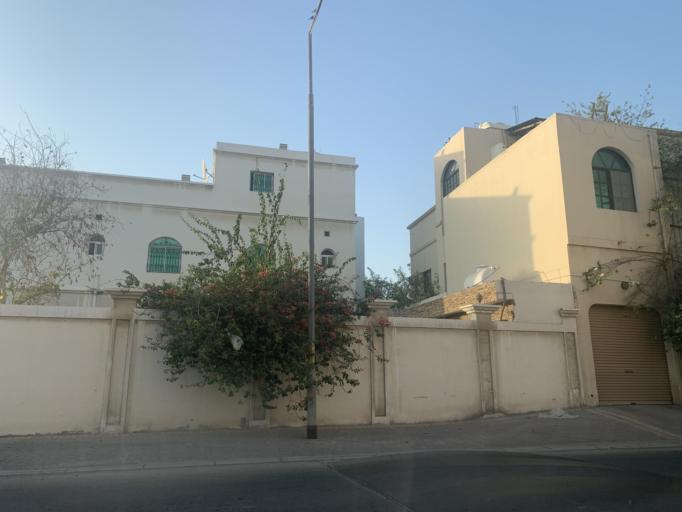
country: BH
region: Manama
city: Jidd Hafs
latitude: 26.2003
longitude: 50.5305
